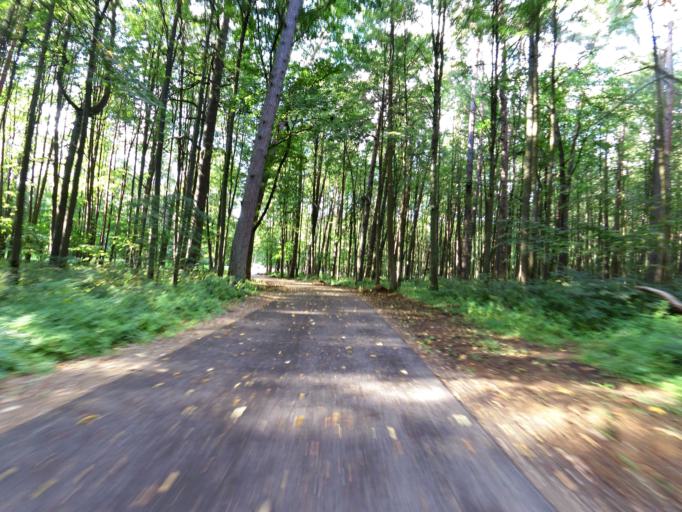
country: LT
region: Vilnius County
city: Vilkpede
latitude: 54.6799
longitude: 25.2354
